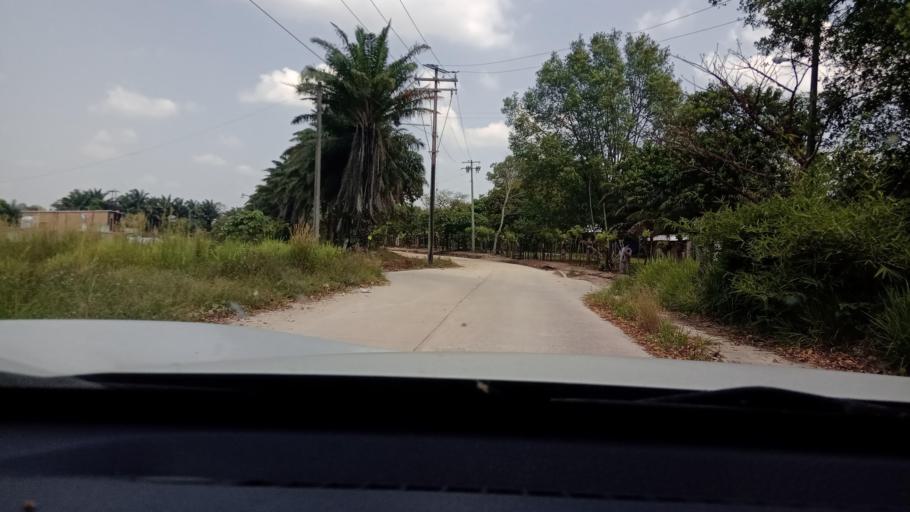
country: MX
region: Veracruz
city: Las Choapas
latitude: 17.9348
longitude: -94.1138
